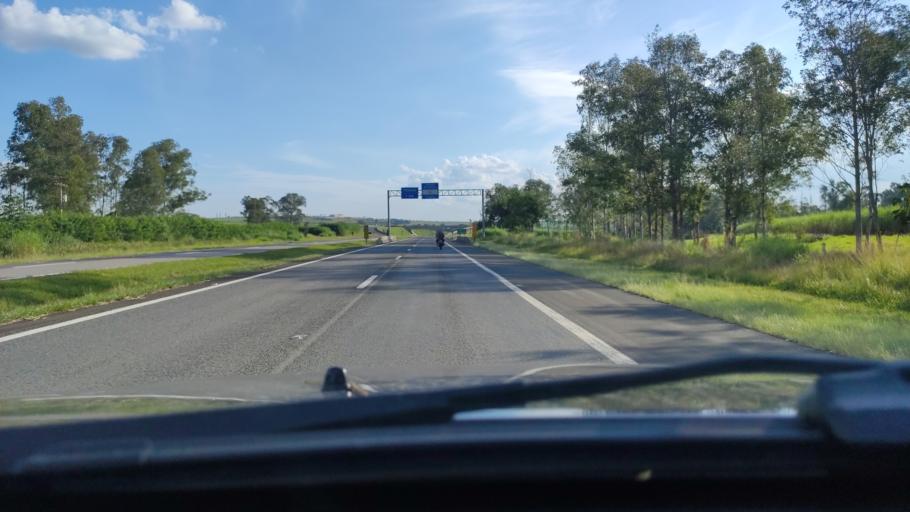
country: BR
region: Sao Paulo
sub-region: Mogi-Mirim
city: Mogi Mirim
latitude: -22.4530
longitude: -46.8926
